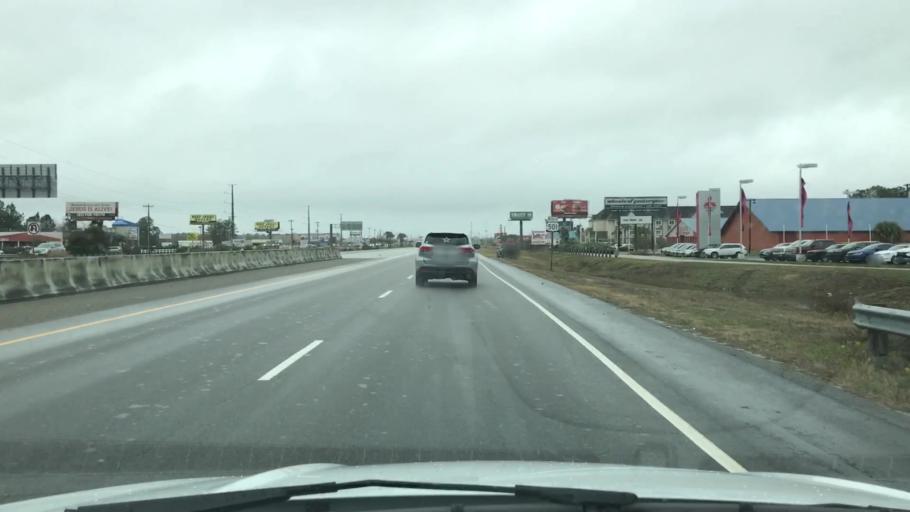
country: US
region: South Carolina
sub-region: Horry County
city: Forestbrook
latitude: 33.7445
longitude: -78.9551
